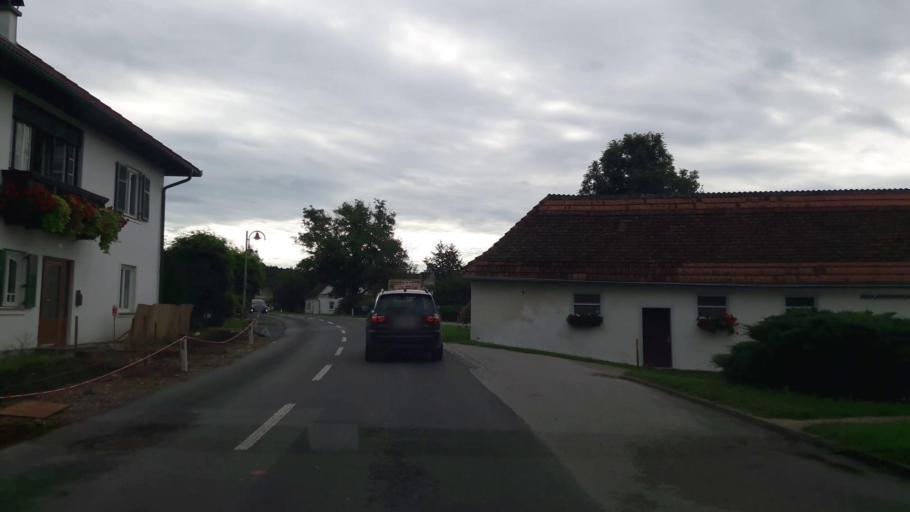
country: AT
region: Styria
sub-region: Politischer Bezirk Hartberg-Fuerstenfeld
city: Ebersdorf
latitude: 47.1983
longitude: 15.9622
